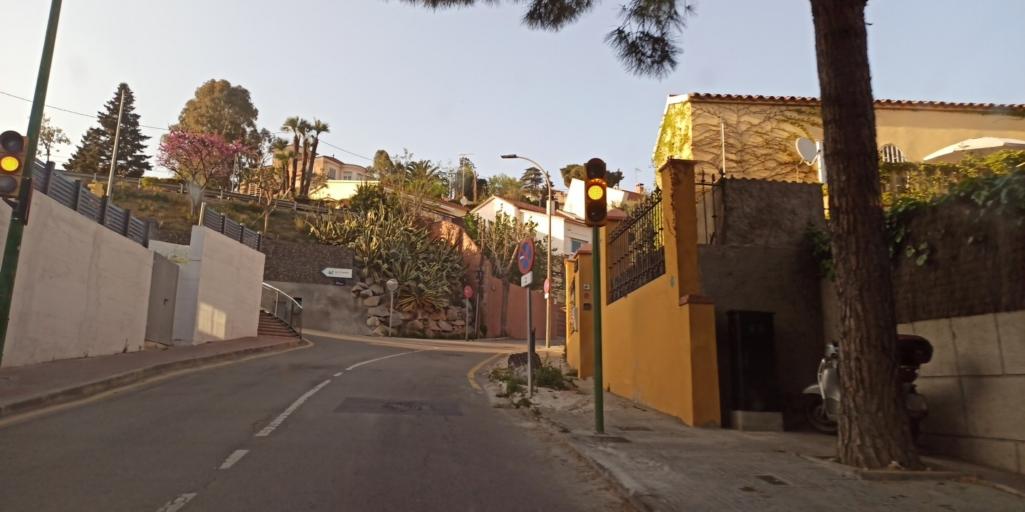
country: ES
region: Catalonia
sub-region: Provincia de Barcelona
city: Sant Just Desvern
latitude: 41.3874
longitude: 2.0849
